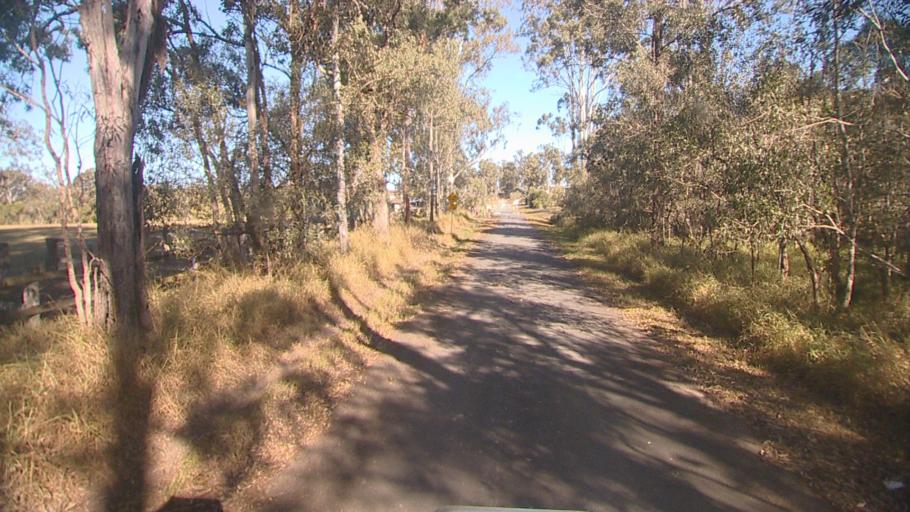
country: AU
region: Queensland
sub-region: Ipswich
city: Springfield Lakes
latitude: -27.7394
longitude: 152.9218
